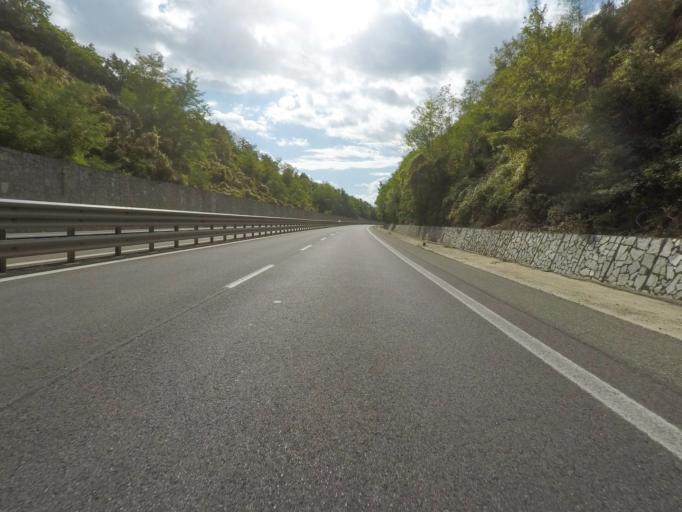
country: IT
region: Tuscany
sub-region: Provincia di Siena
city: Serre di Rapolano
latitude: 43.2812
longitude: 11.6283
